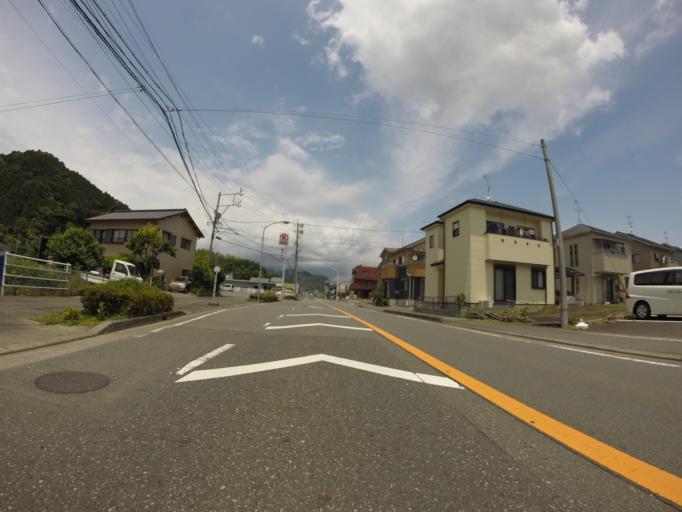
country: JP
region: Shizuoka
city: Shizuoka-shi
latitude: 34.9647
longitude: 138.3565
